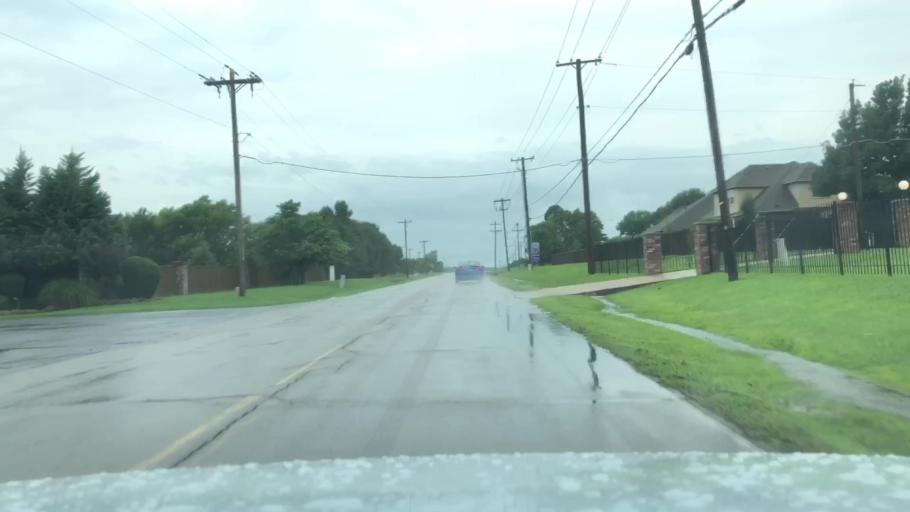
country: US
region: Oklahoma
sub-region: Tulsa County
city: Jenks
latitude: 36.0028
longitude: -96.0006
